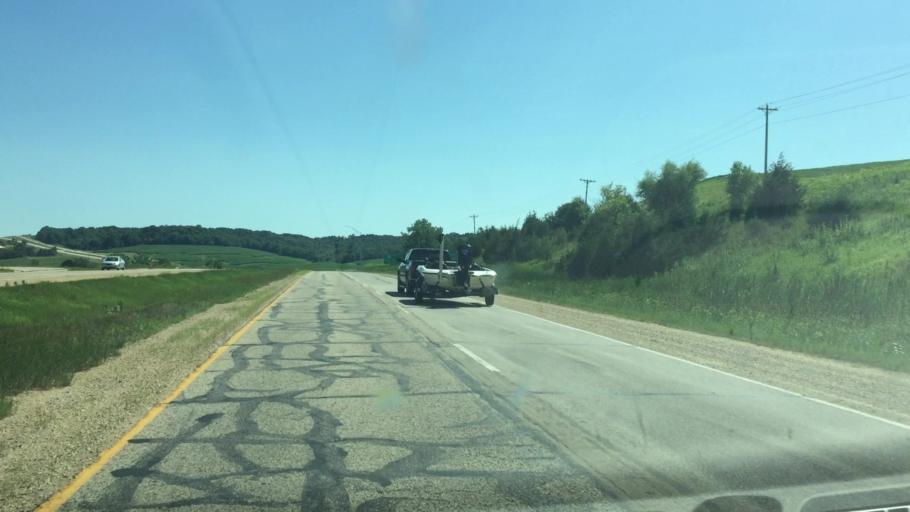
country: US
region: Iowa
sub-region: Dubuque County
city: Dubuque
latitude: 42.4256
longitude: -90.6921
